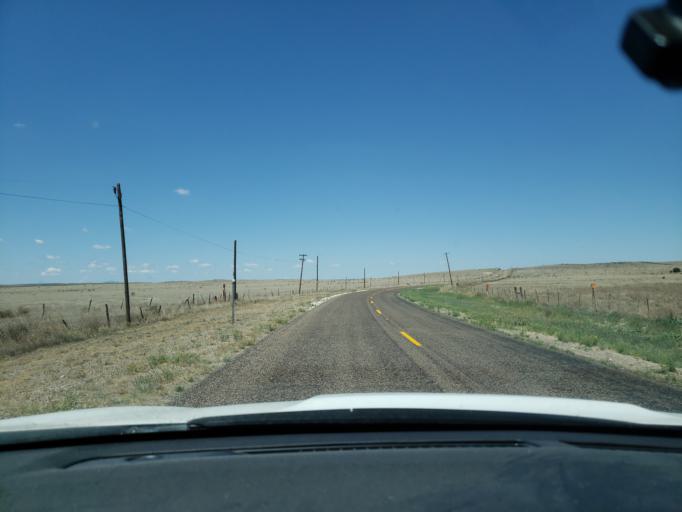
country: US
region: Texas
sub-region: Presidio County
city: Marfa
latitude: 30.2900
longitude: -104.0408
